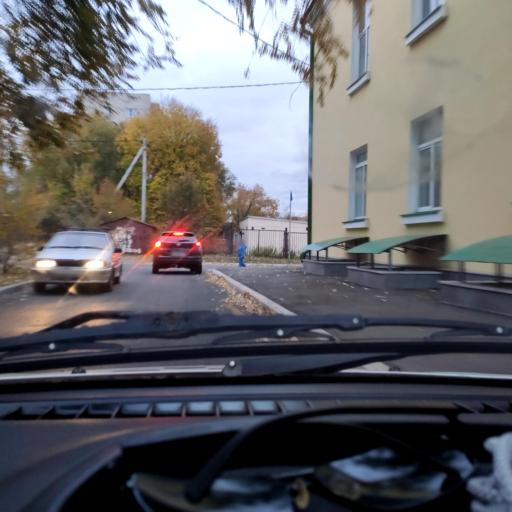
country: RU
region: Samara
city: Zhigulevsk
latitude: 53.4635
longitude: 49.5340
